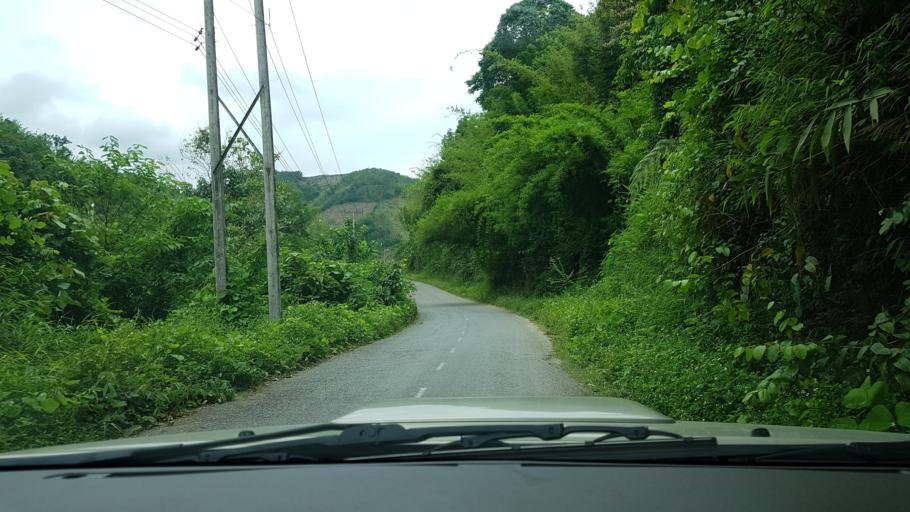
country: LA
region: Phongsali
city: Khoa
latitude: 21.0567
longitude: 102.3913
